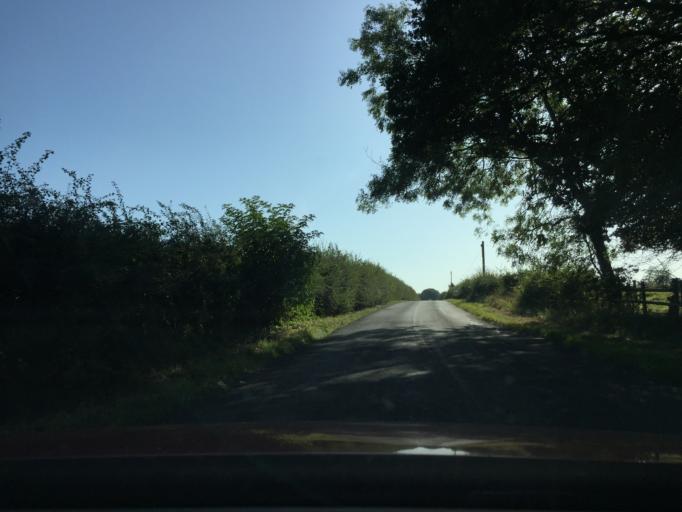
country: GB
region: England
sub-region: Leicestershire
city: Houghton on the Hill
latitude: 52.6438
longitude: -0.9774
